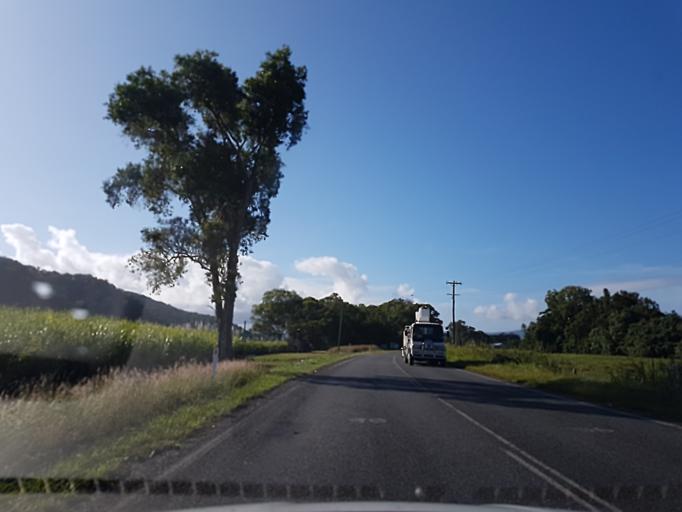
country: AU
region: Queensland
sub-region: Cairns
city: Port Douglas
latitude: -16.3422
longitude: 145.4090
